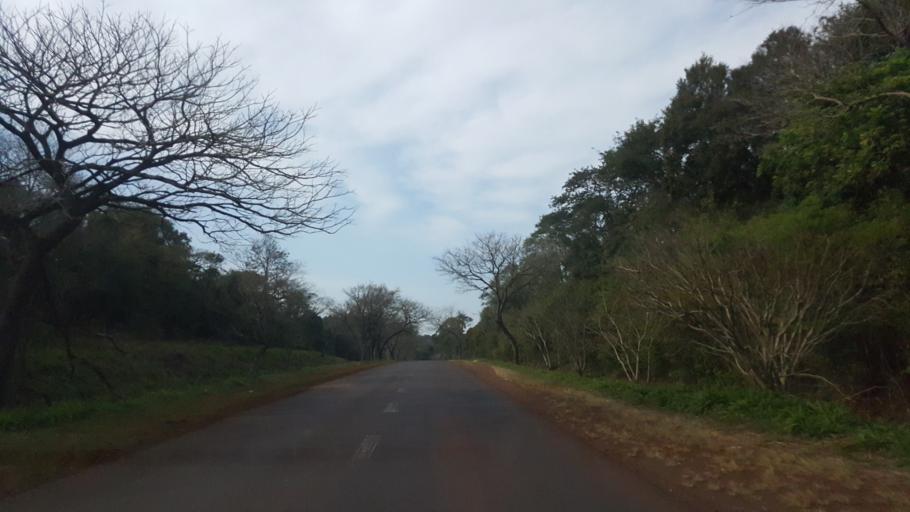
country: AR
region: Misiones
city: Capiovi
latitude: -26.9367
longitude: -55.0825
